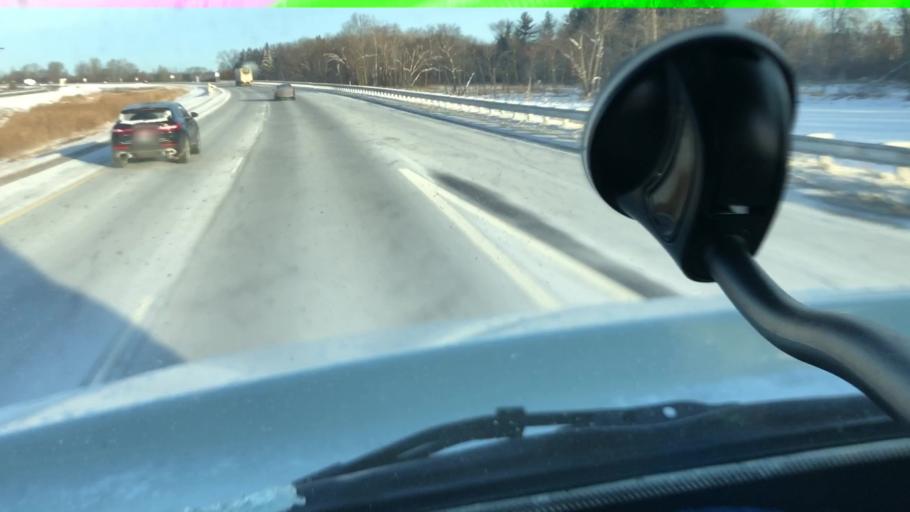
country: US
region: Wisconsin
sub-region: Columbia County
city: Portage
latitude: 43.5168
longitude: -89.5259
